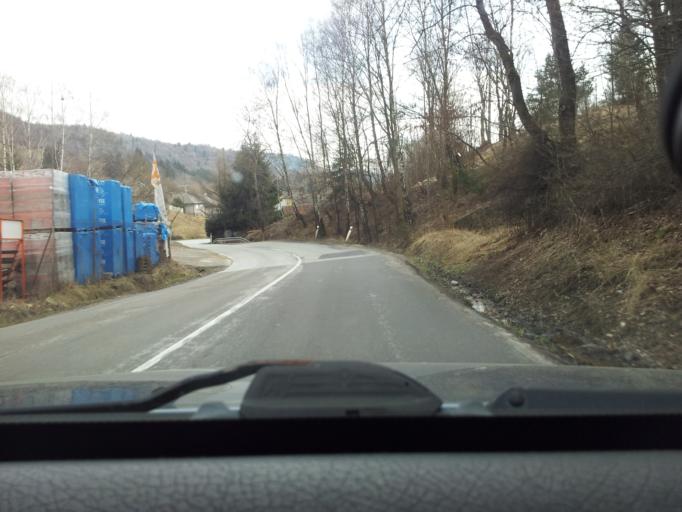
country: SK
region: Banskobystricky
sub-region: Okres Ziar nad Hronom
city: Kremnica
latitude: 48.7359
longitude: 18.9095
